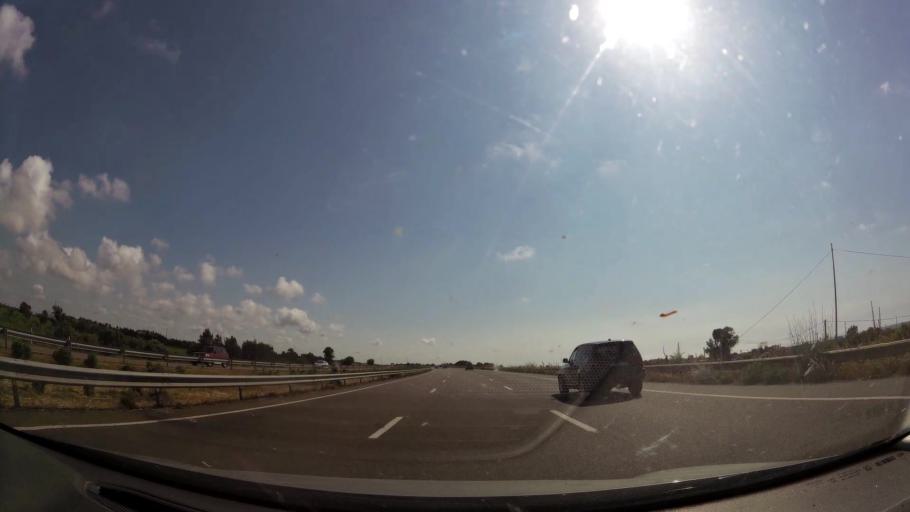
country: MA
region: Rabat-Sale-Zemmour-Zaer
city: Skhirat
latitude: 33.8500
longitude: -7.0729
